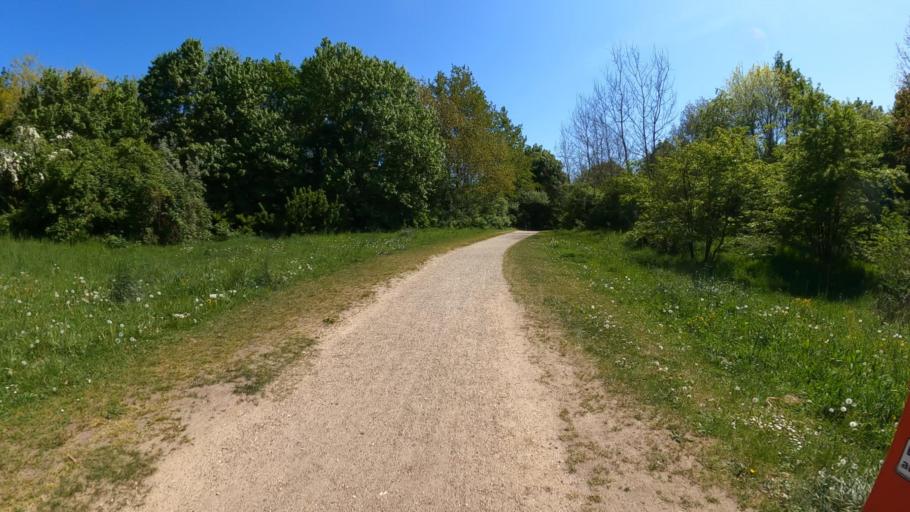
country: DE
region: Hamburg
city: Eidelstedt
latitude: 53.5760
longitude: 9.8739
